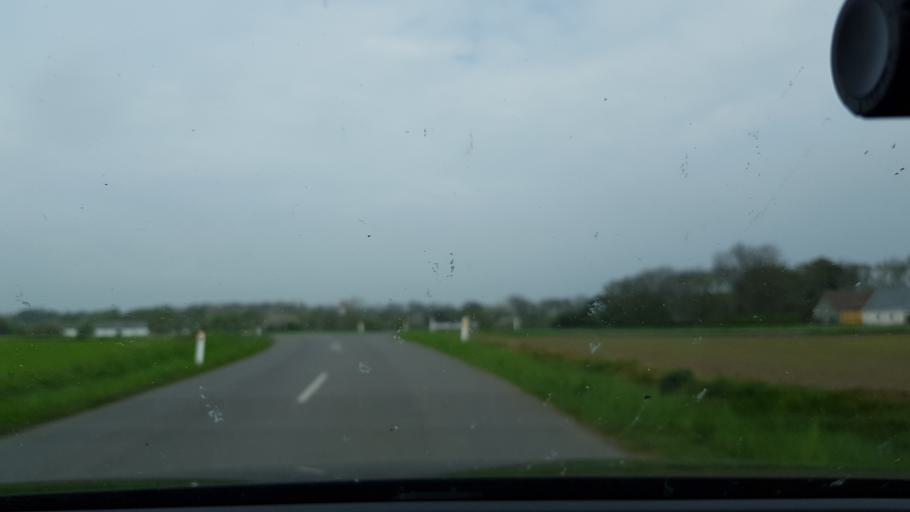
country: DK
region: Capital Region
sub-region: Bornholm Kommune
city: Nexo
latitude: 55.0221
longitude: 15.0972
